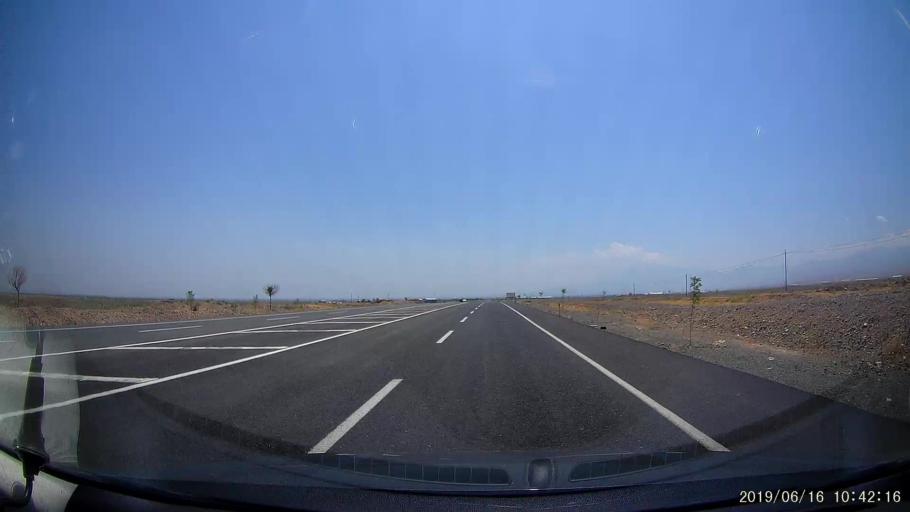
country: AM
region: Armavir
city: Shenavan
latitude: 40.0432
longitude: 43.8031
